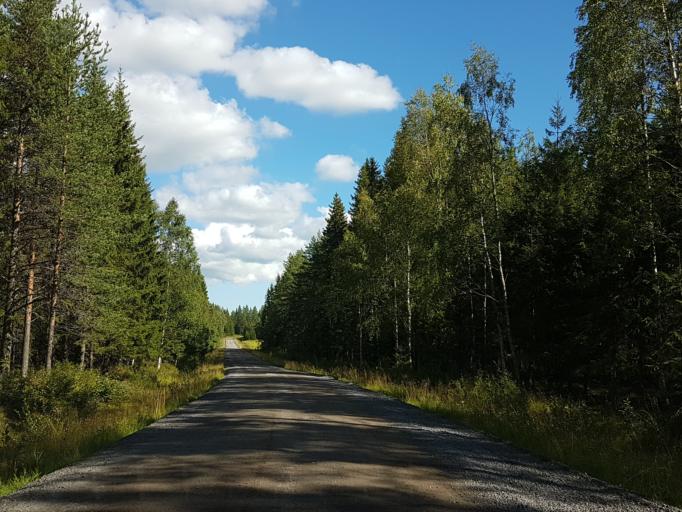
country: SE
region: Vaesterbotten
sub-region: Skelleftea Kommun
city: Burtraesk
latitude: 64.2954
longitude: 20.4977
